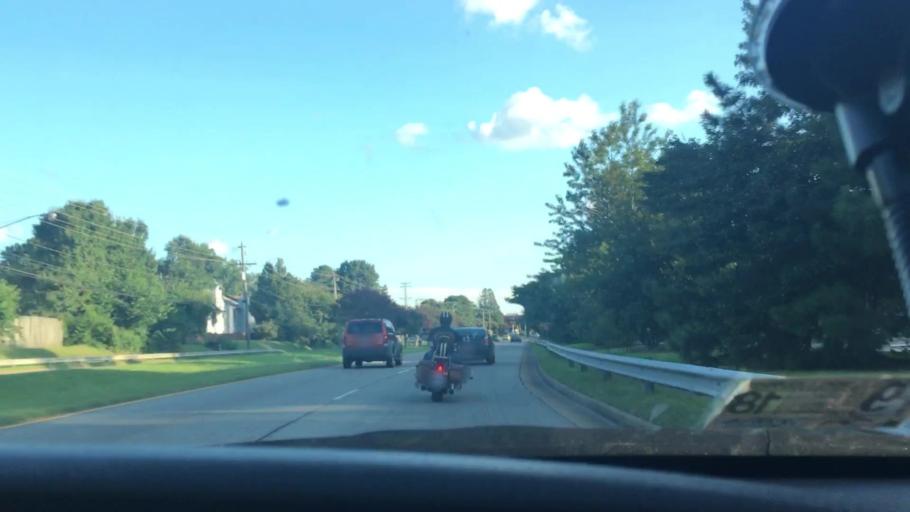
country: US
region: Virginia
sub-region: City of Chesapeake
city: Chesapeake
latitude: 36.8818
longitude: -76.1332
